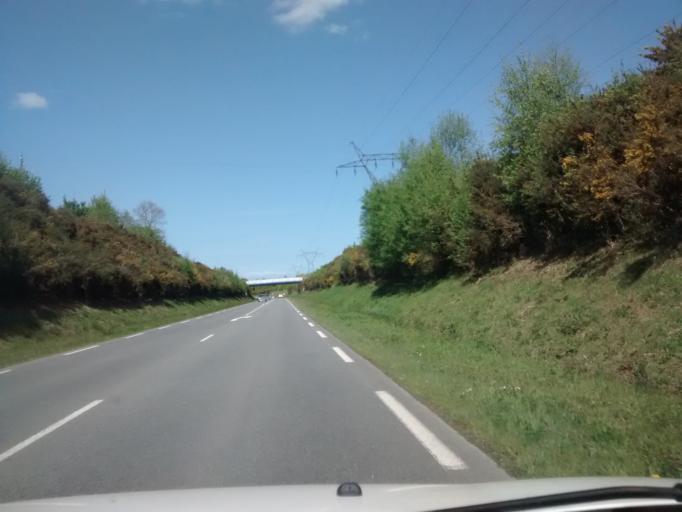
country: FR
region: Brittany
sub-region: Departement des Cotes-d'Armor
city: Pleslin-Trigavou
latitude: 48.5315
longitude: -2.0378
